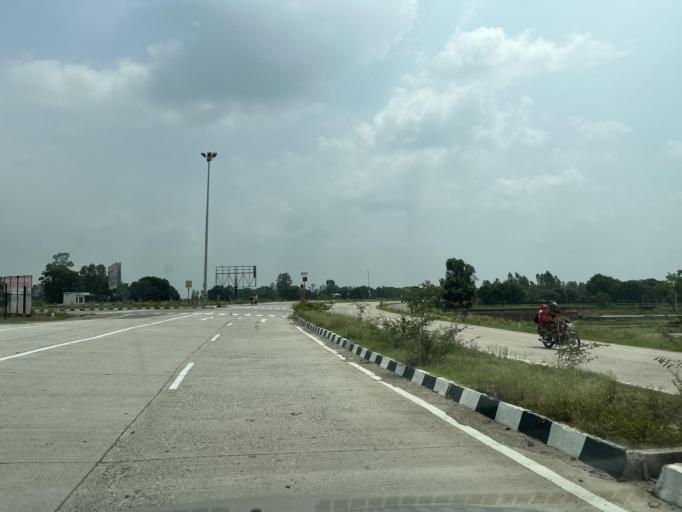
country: IN
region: Uttar Pradesh
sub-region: Bijnor
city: Nagina
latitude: 29.4244
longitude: 78.4434
